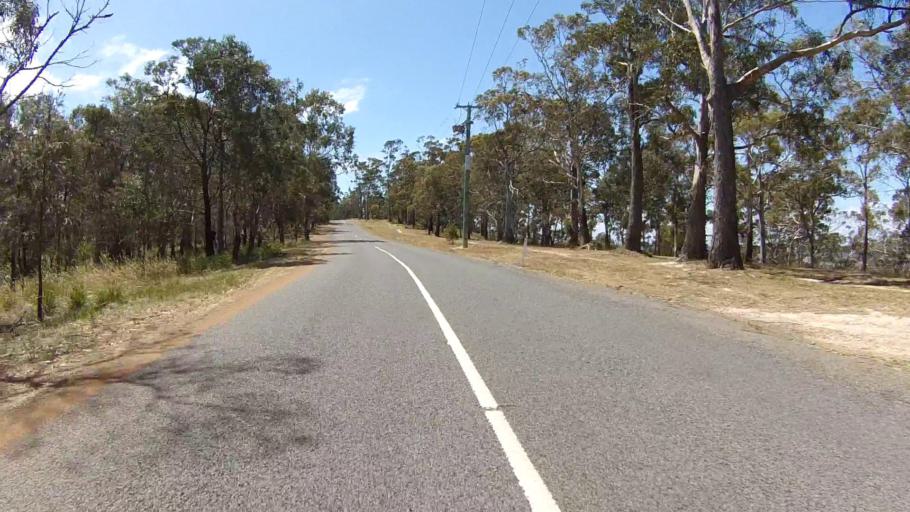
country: AU
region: Tasmania
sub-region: Clarence
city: Sandford
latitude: -43.0190
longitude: 147.4817
